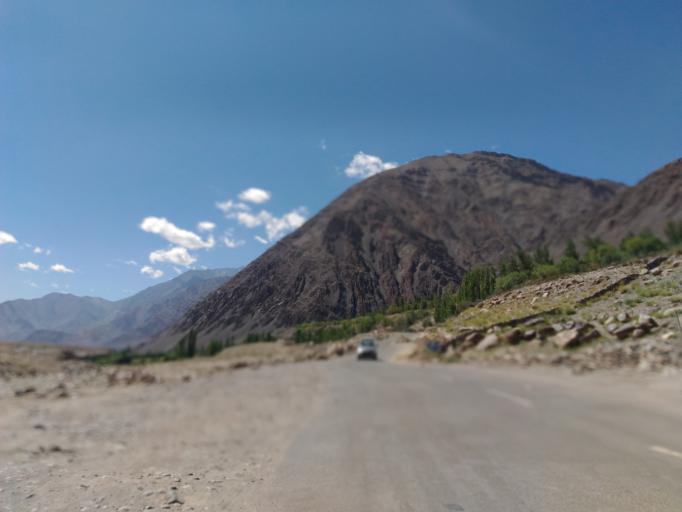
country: IN
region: Kashmir
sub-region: Ladakh
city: Leh
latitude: 33.8273
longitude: 77.8186
